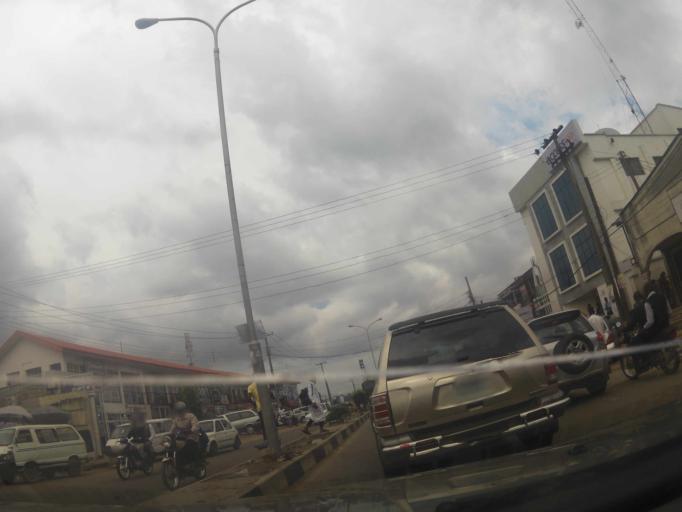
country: NG
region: Oyo
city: Ibadan
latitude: 7.3935
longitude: 3.8838
